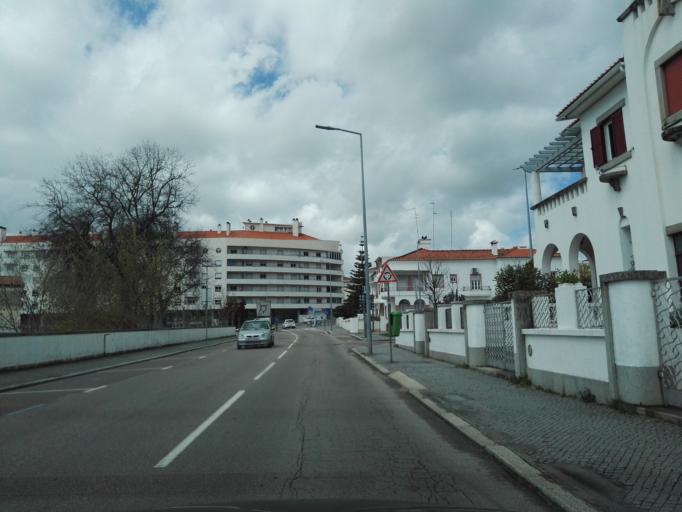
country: PT
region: Portalegre
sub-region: Portalegre
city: Portalegre
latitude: 39.2995
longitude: -7.4306
